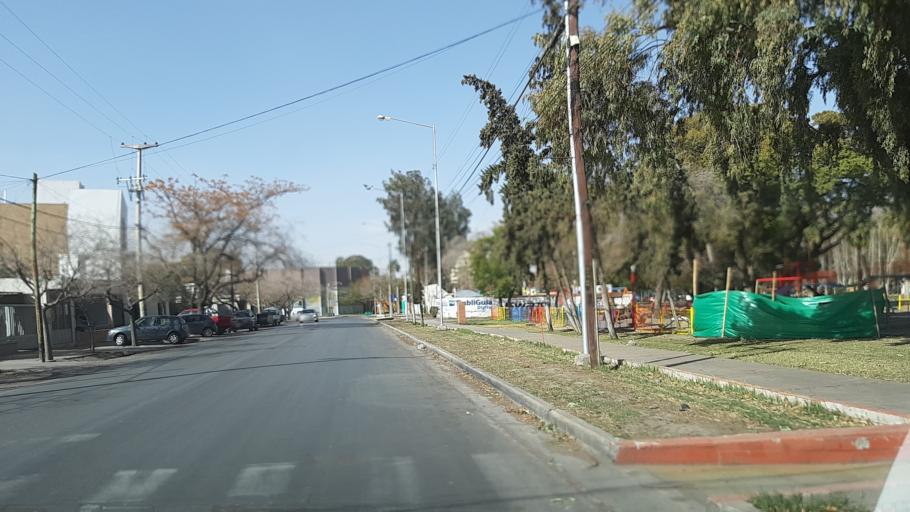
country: AR
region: San Juan
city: San Juan
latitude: -31.5316
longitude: -68.5403
